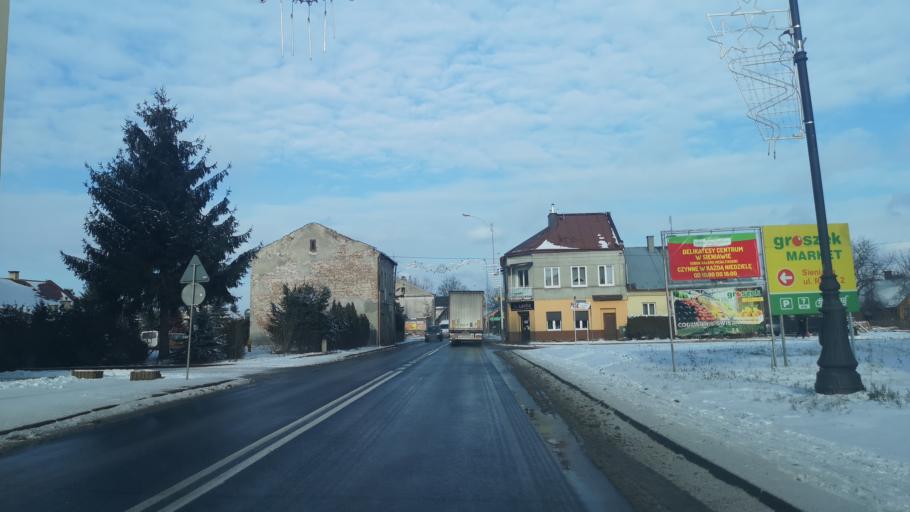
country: PL
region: Subcarpathian Voivodeship
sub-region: Powiat przeworski
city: Sieniawa
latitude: 50.1786
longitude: 22.6098
